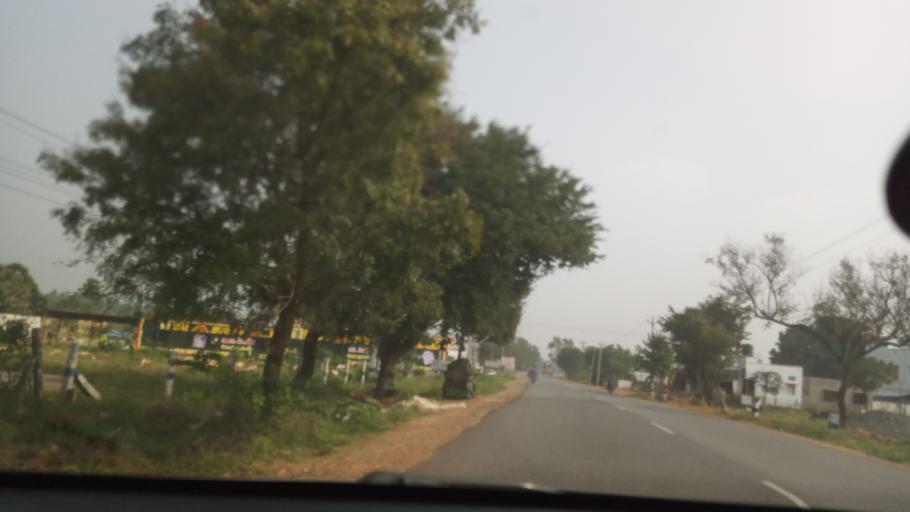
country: IN
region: Tamil Nadu
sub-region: Erode
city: Punjai Puliyampatti
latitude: 11.3351
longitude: 77.1550
